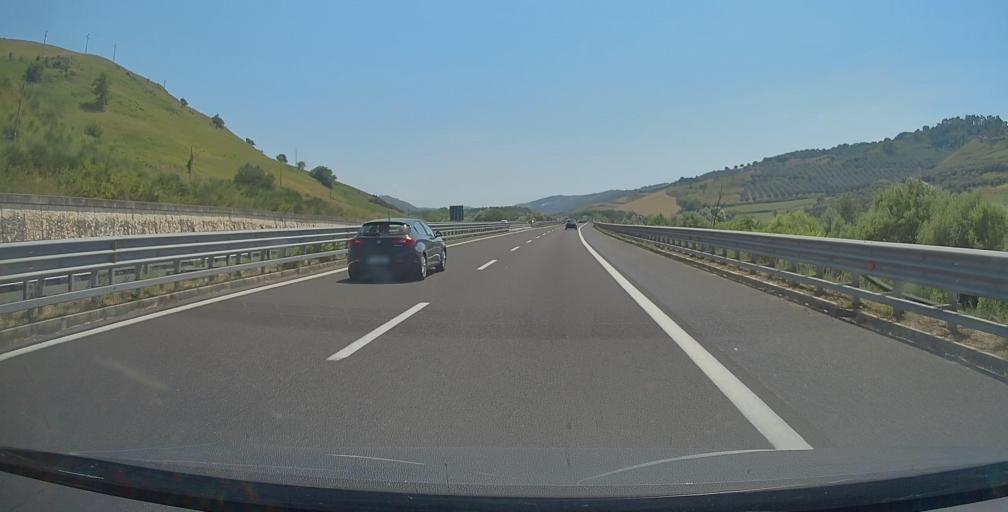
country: IT
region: Calabria
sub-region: Provincia di Vibo-Valentia
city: Francica
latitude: 38.6163
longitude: 16.1562
